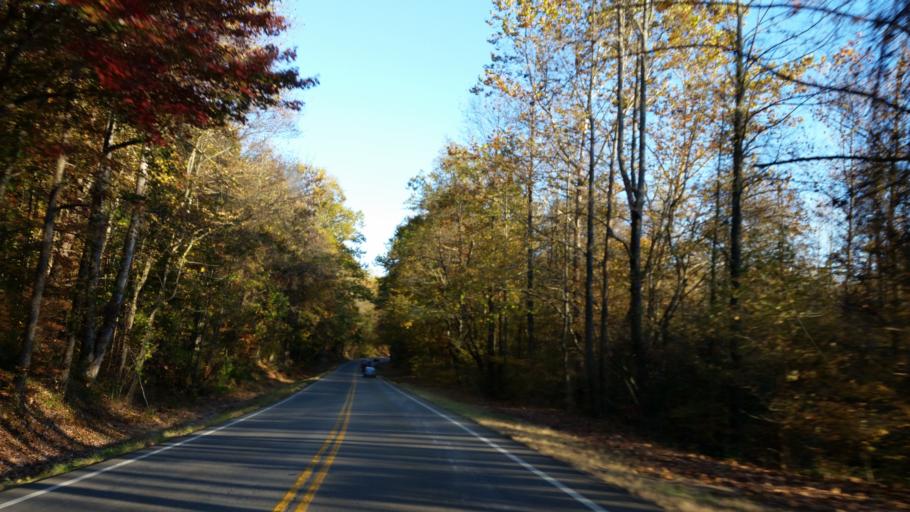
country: US
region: Georgia
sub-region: Pickens County
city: Jasper
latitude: 34.5636
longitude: -84.3055
